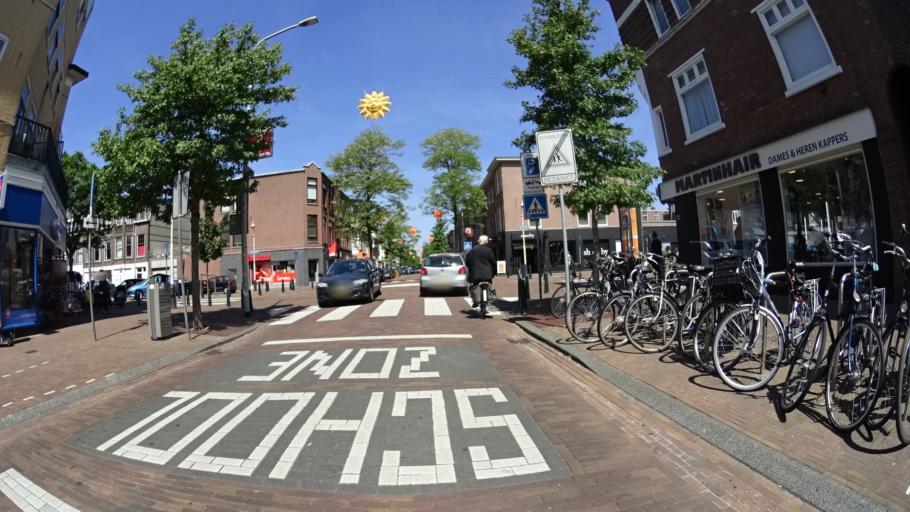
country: NL
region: South Holland
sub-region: Gemeente Den Haag
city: Scheveningen
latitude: 52.0787
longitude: 4.2694
